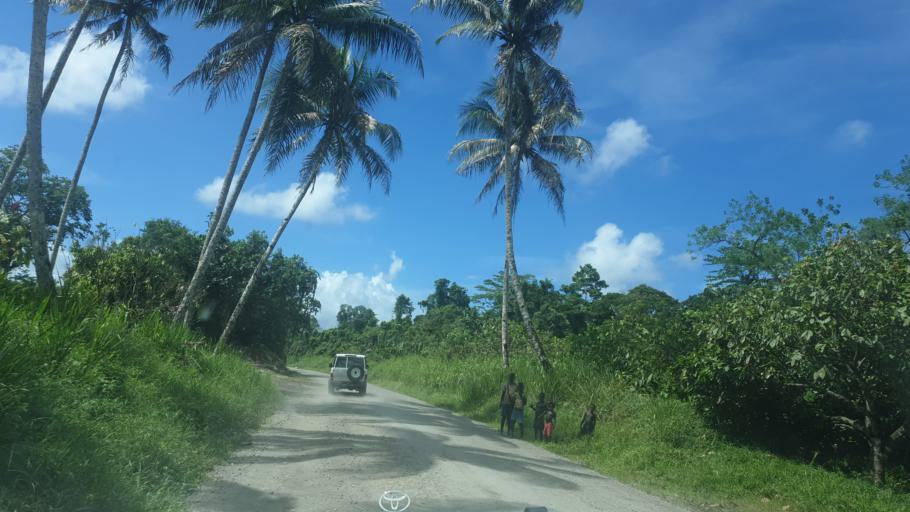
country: PG
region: Bougainville
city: Panguna
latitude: -6.7385
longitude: 155.6653
